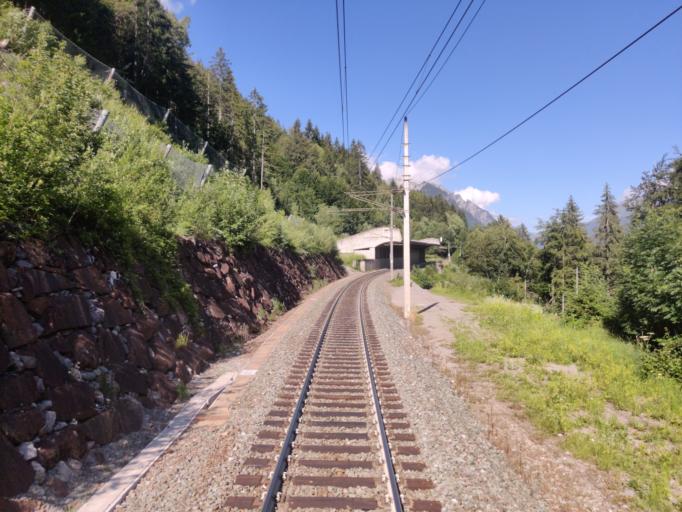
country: AT
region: Vorarlberg
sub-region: Politischer Bezirk Bludenz
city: Dalaas
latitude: 47.1284
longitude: 10.0126
